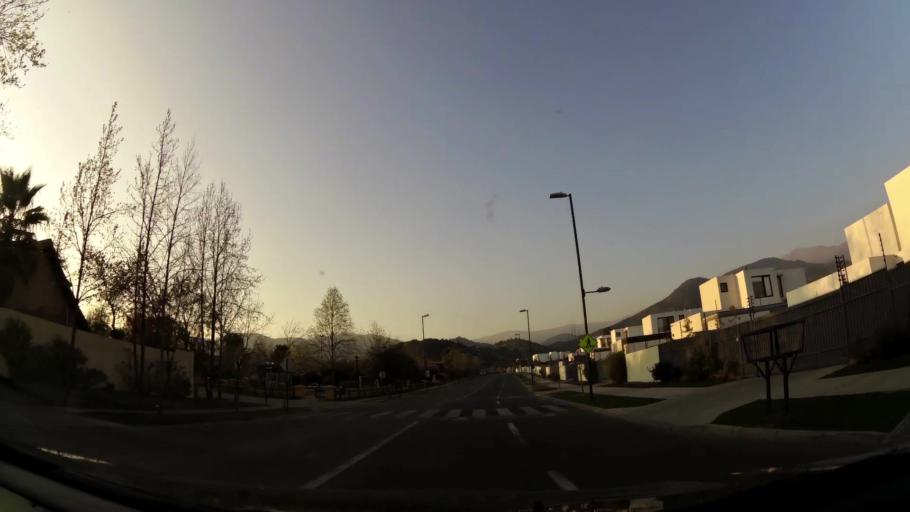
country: CL
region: Santiago Metropolitan
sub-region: Provincia de Chacabuco
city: Chicureo Abajo
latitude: -33.3263
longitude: -70.5387
